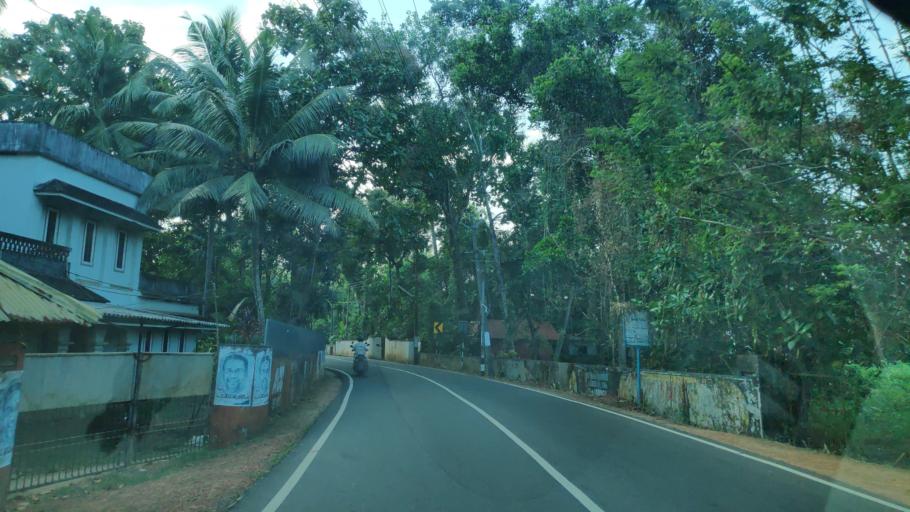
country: IN
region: Kerala
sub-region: Alappuzha
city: Shertallai
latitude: 9.6786
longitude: 76.3891
